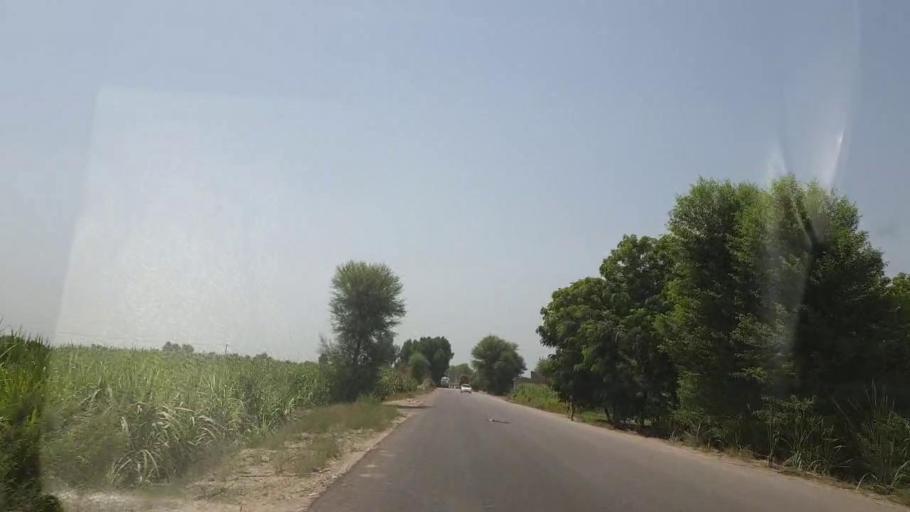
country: PK
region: Sindh
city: Ranipur
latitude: 27.2924
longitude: 68.6045
